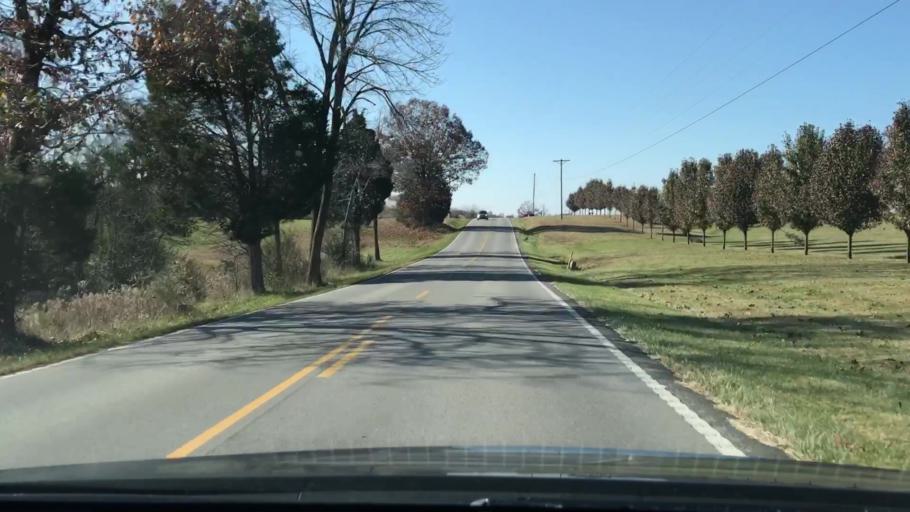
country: US
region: Kentucky
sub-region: Edmonson County
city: Brownsville
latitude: 37.3290
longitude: -86.2589
